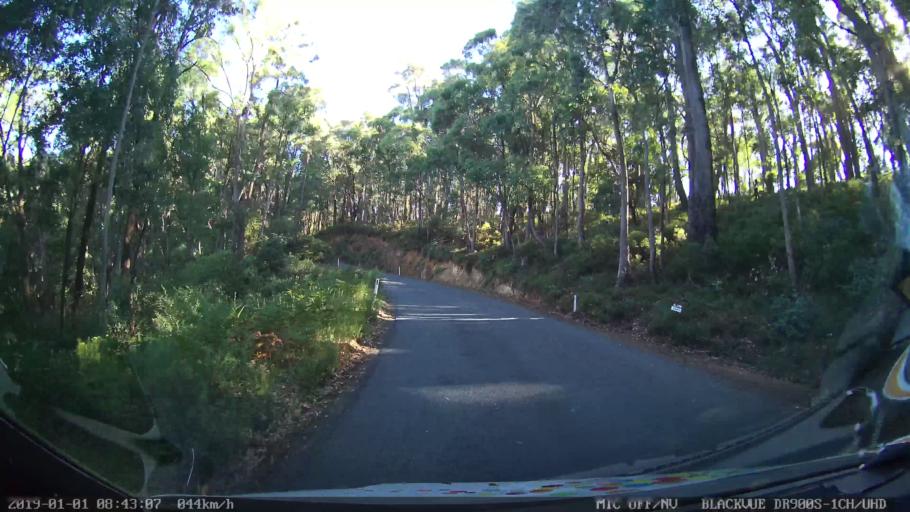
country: AU
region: New South Wales
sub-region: Snowy River
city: Jindabyne
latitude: -36.3196
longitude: 148.1932
